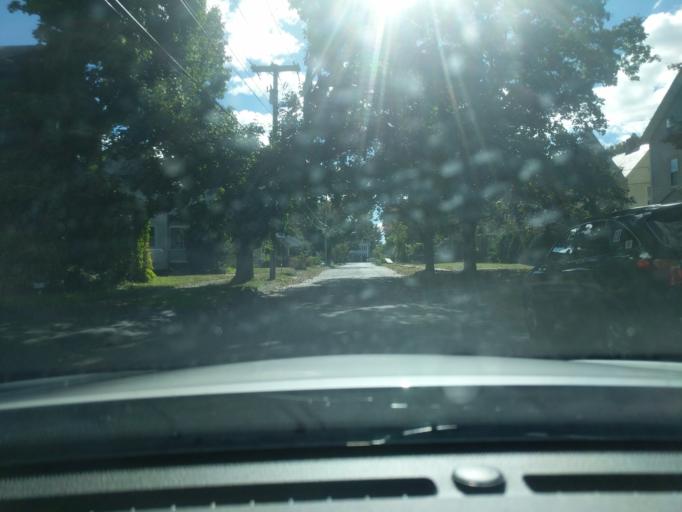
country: US
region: Massachusetts
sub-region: Hampden County
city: Westfield
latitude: 42.1270
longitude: -72.7517
